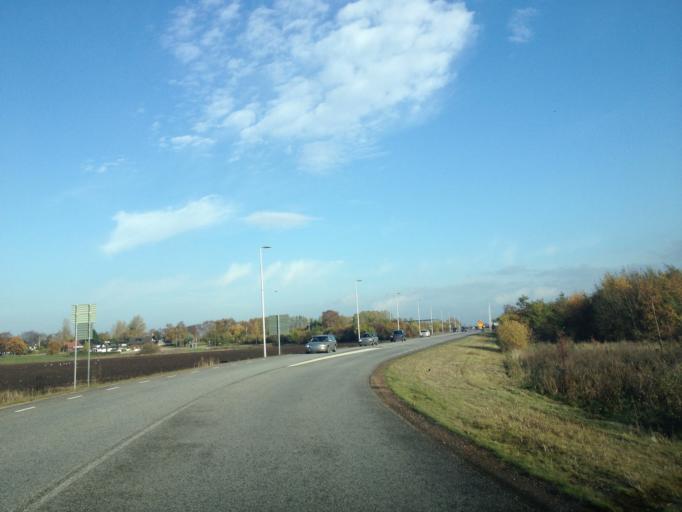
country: SE
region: Skane
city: Bjarred
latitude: 55.7270
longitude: 13.0278
